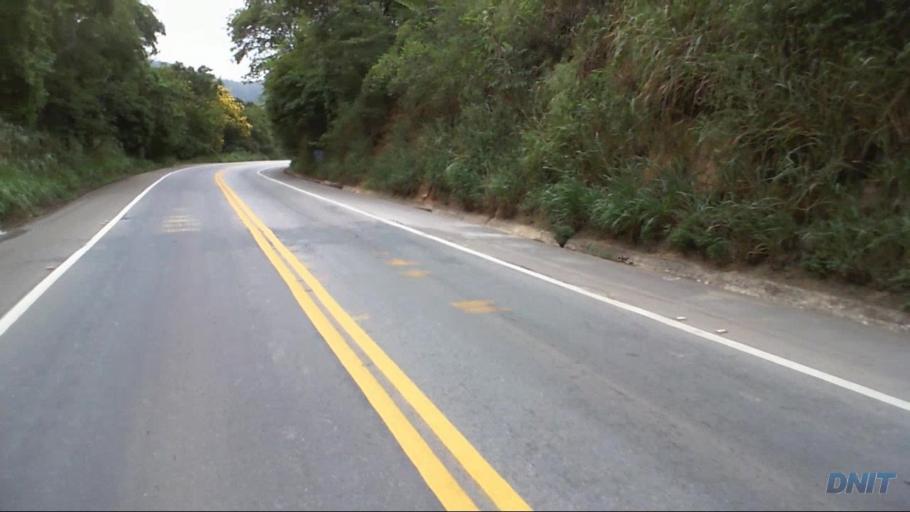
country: BR
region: Minas Gerais
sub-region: Timoteo
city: Timoteo
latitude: -19.5704
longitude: -42.7131
